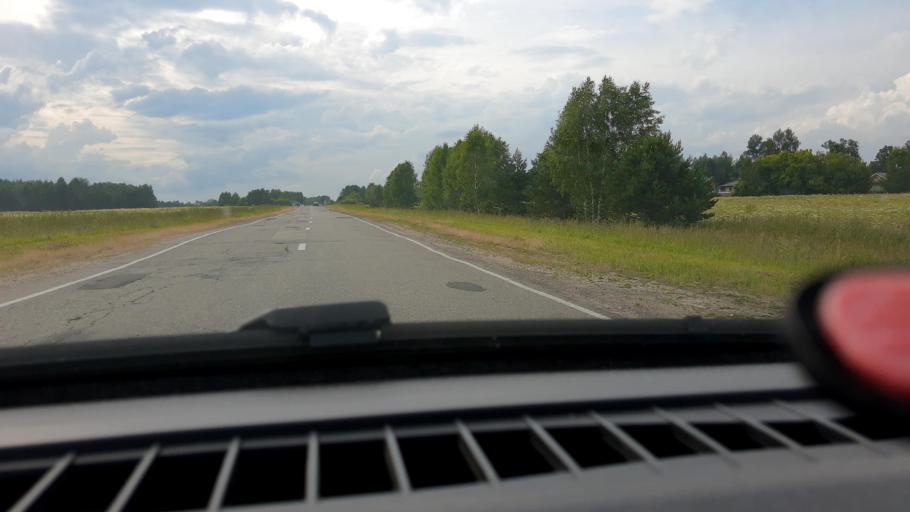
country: RU
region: Nizjnij Novgorod
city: Neklyudovo
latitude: 56.5033
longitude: 43.9822
